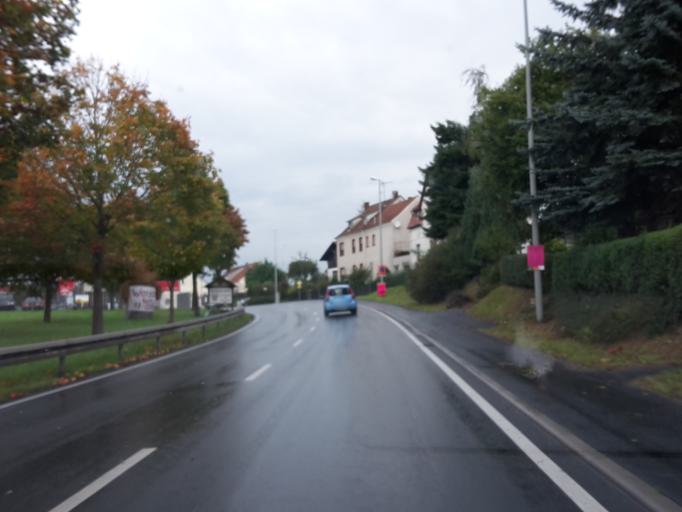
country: DE
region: Hesse
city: Bad Camberg
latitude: 50.2807
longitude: 8.2805
